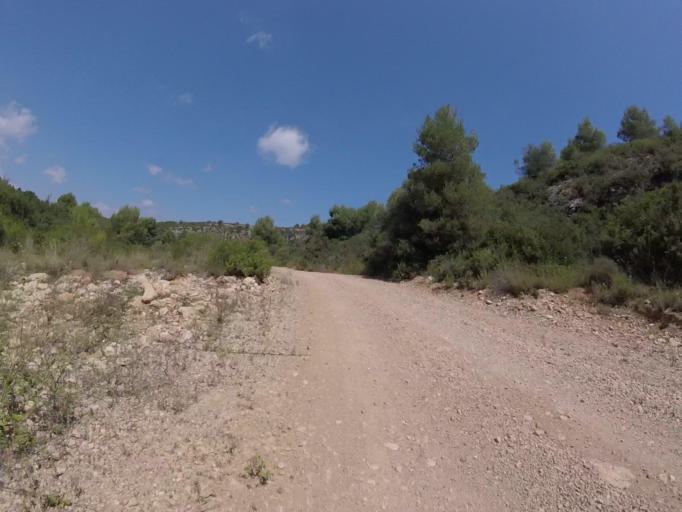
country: ES
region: Valencia
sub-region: Provincia de Castello
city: Torreblanca
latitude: 40.2195
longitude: 0.1489
